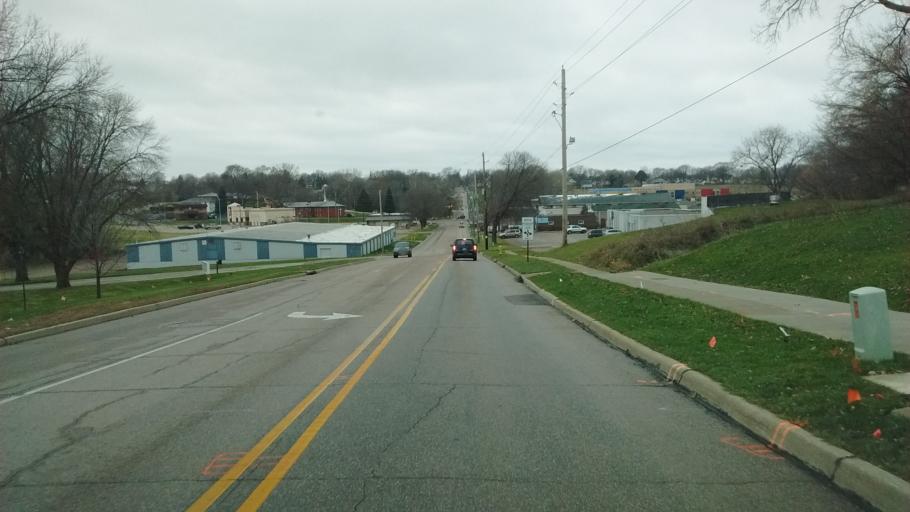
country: US
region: Iowa
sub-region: Woodbury County
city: Sioux City
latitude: 42.4792
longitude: -96.3473
